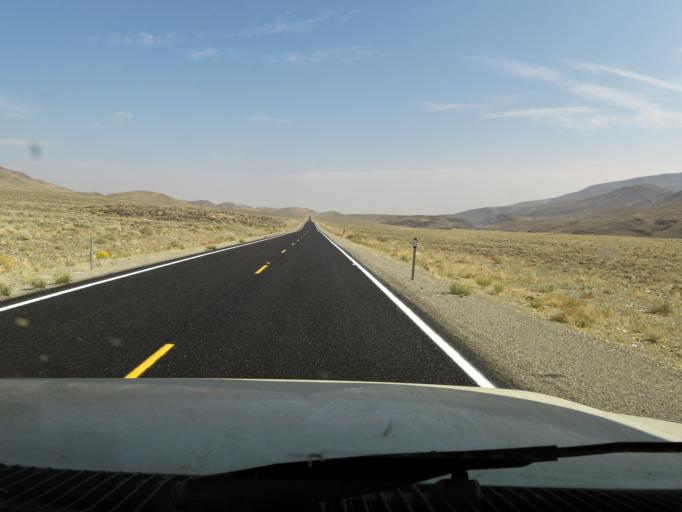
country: US
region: California
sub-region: Inyo County
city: Dixon Lane-Meadow Creek
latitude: 38.0048
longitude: -118.1566
